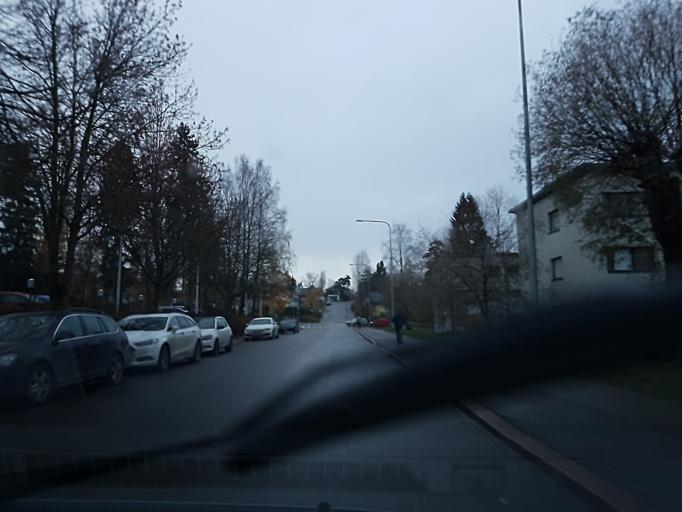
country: FI
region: Uusimaa
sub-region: Helsinki
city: Vantaa
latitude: 60.2379
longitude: 25.1149
